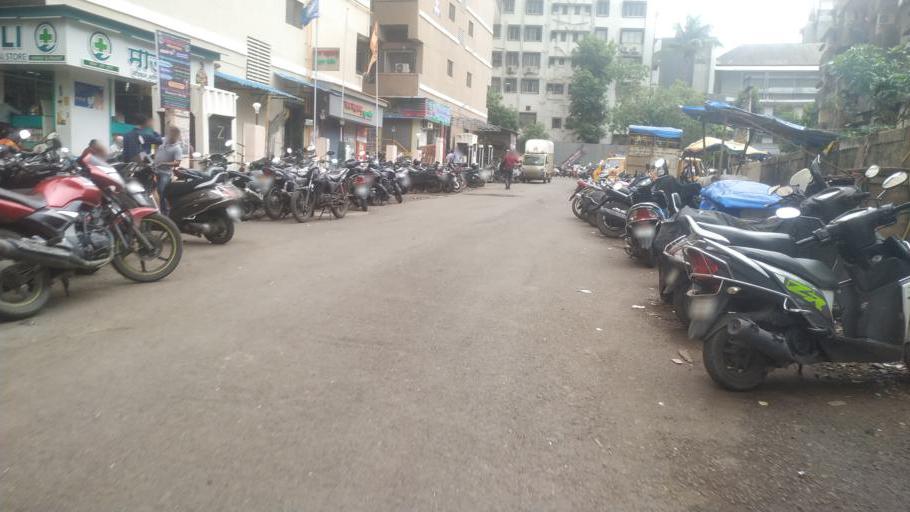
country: IN
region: Maharashtra
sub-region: Mumbai Suburban
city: Mumbai
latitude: 19.0047
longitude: 72.8483
